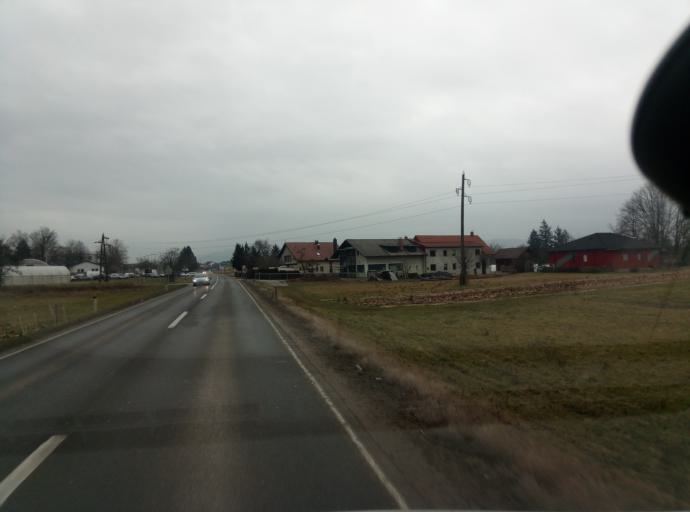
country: SI
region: Dol pri Ljubljani
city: Dol pri Ljubljani
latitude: 46.0918
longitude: 14.5708
